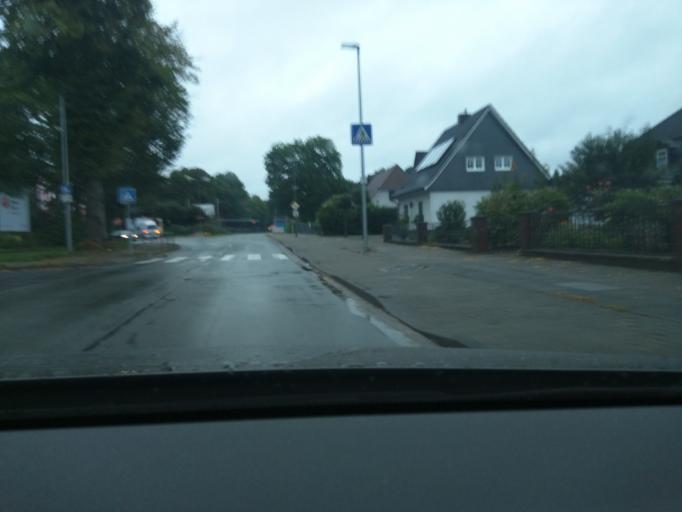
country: DE
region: Schleswig-Holstein
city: Lauenburg
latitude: 53.3795
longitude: 10.5472
